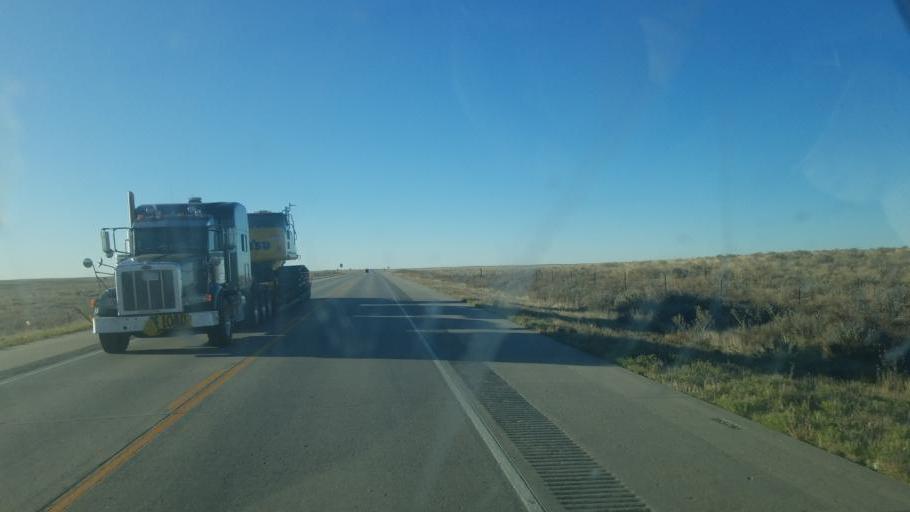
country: US
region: Colorado
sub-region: Kiowa County
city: Eads
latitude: 38.5811
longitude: -102.7859
